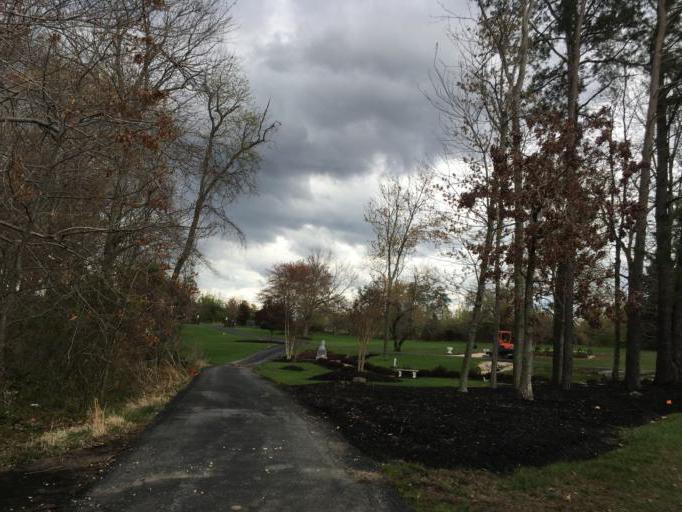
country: US
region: Maryland
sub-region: Howard County
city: Hanover
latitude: 39.1738
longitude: -76.7115
